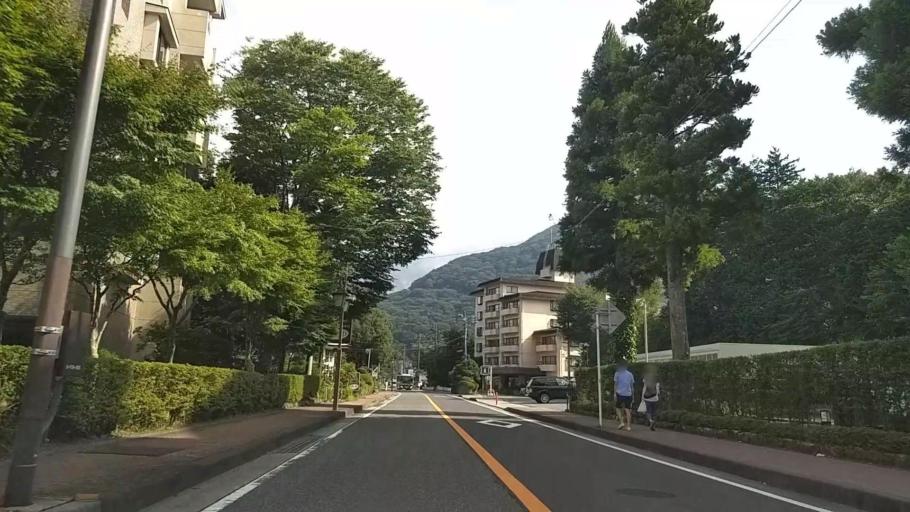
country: JP
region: Shizuoka
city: Gotemba
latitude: 35.2690
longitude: 139.0120
